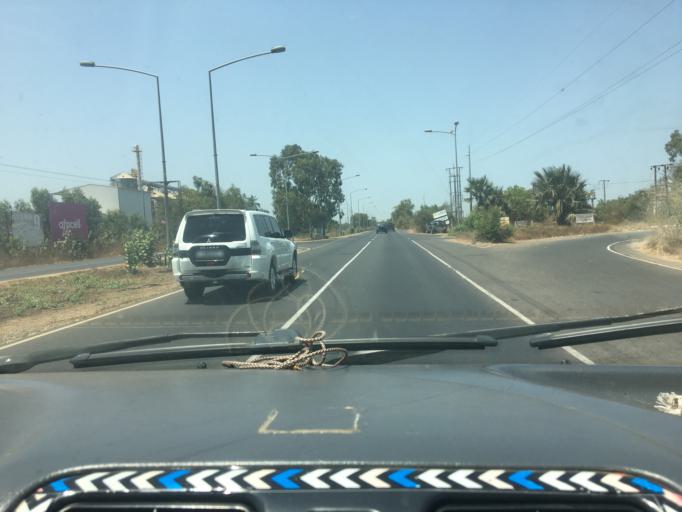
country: GM
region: Banjul
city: Bakau
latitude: 13.4668
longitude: -16.6508
